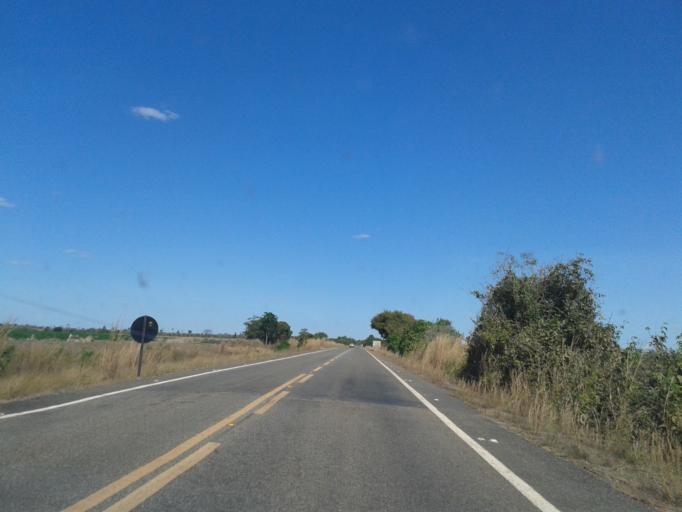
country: BR
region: Goias
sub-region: Sao Miguel Do Araguaia
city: Sao Miguel do Araguaia
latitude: -13.6135
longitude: -50.3195
